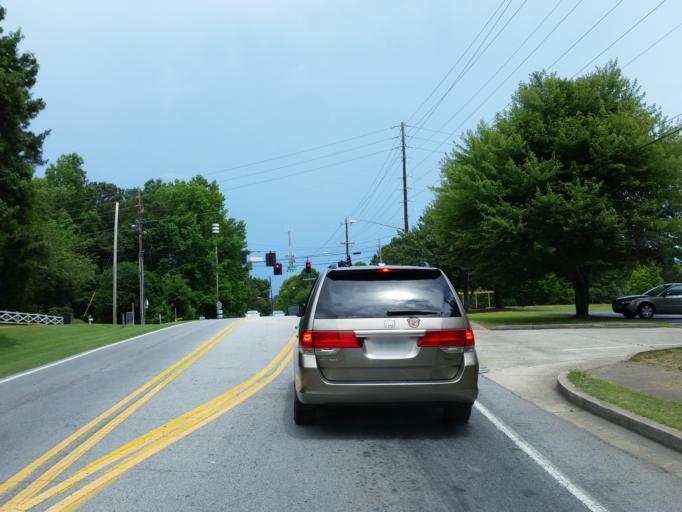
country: US
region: Georgia
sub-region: Fulton County
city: Roswell
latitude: 34.0652
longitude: -84.3842
